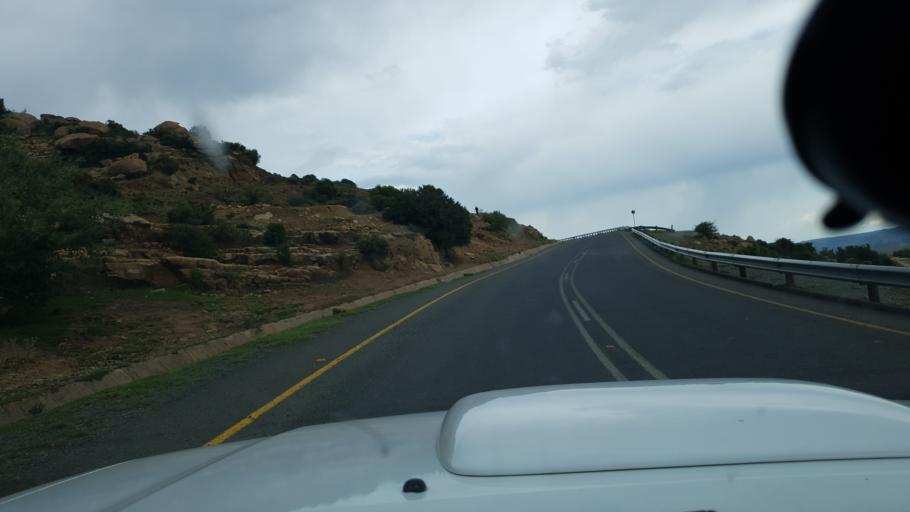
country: LS
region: Maseru
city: Maseru
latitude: -29.4629
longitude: 27.4911
